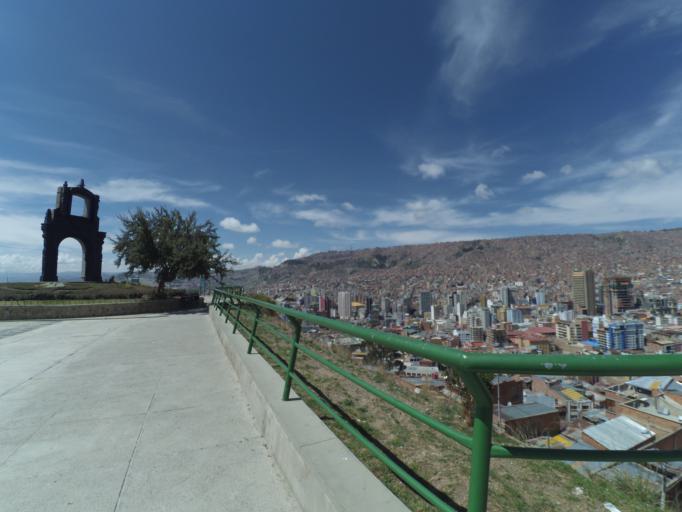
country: BO
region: La Paz
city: La Paz
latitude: -16.4950
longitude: -68.1275
